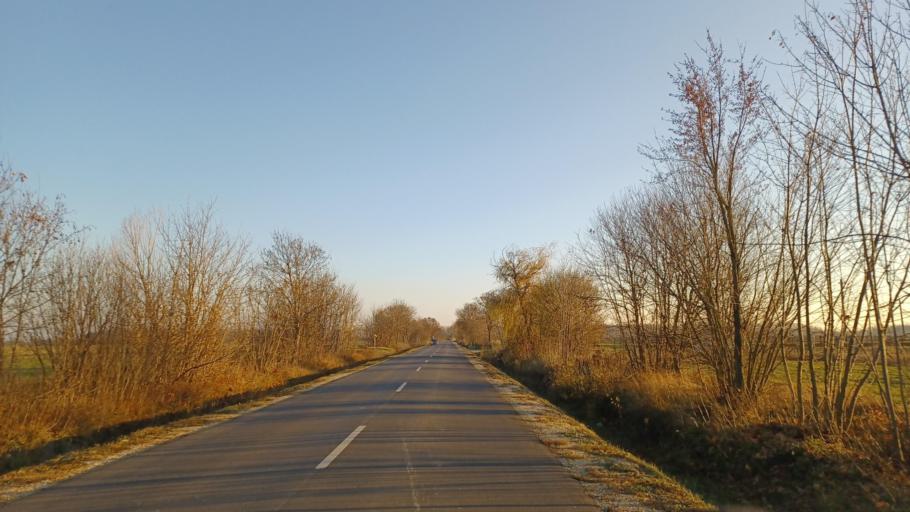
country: HU
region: Tolna
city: Fadd
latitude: 46.4927
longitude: 18.8334
